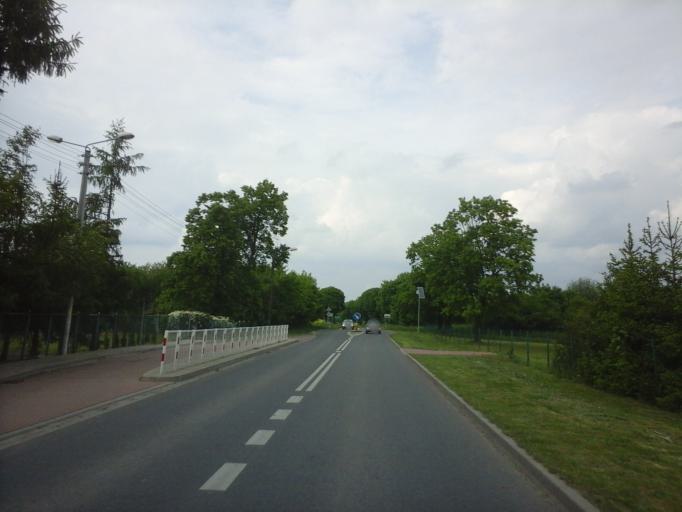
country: PL
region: West Pomeranian Voivodeship
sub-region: Powiat choszczenski
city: Choszczno
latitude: 53.1329
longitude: 15.3781
